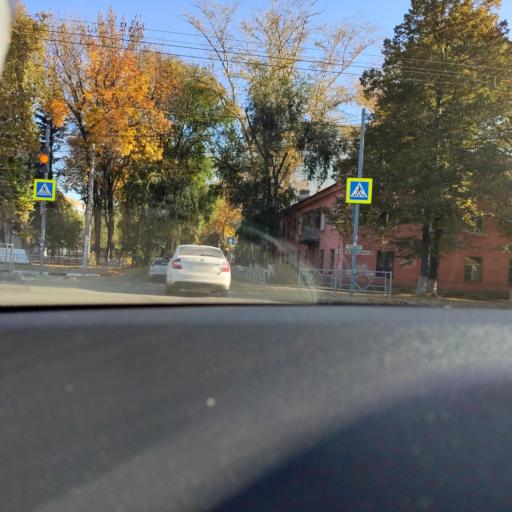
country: RU
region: Samara
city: Samara
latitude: 53.2274
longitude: 50.2523
